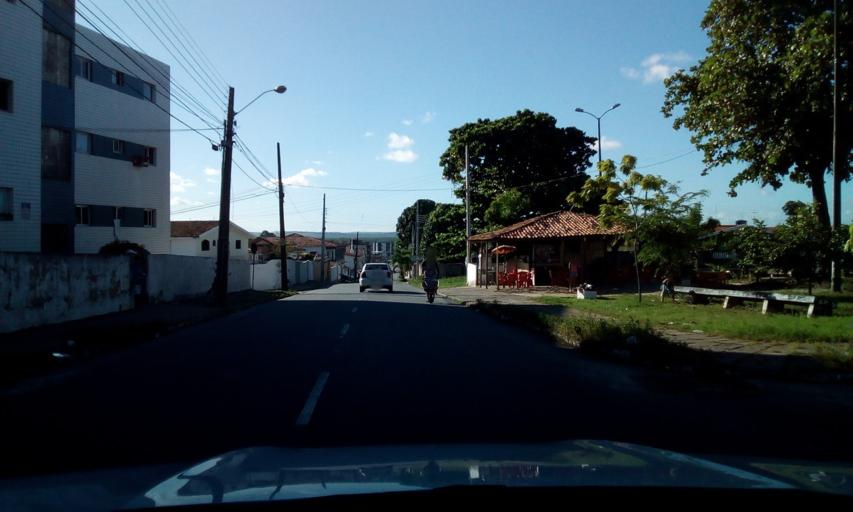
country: BR
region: Paraiba
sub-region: Joao Pessoa
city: Joao Pessoa
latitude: -7.1052
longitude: -34.8584
